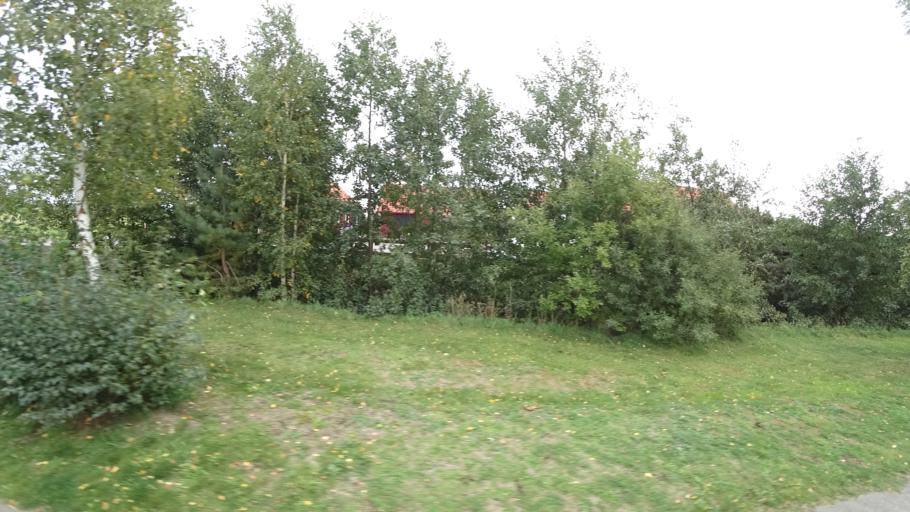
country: SE
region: Skane
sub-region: Kavlinge Kommun
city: Hofterup
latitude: 55.7997
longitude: 12.9964
